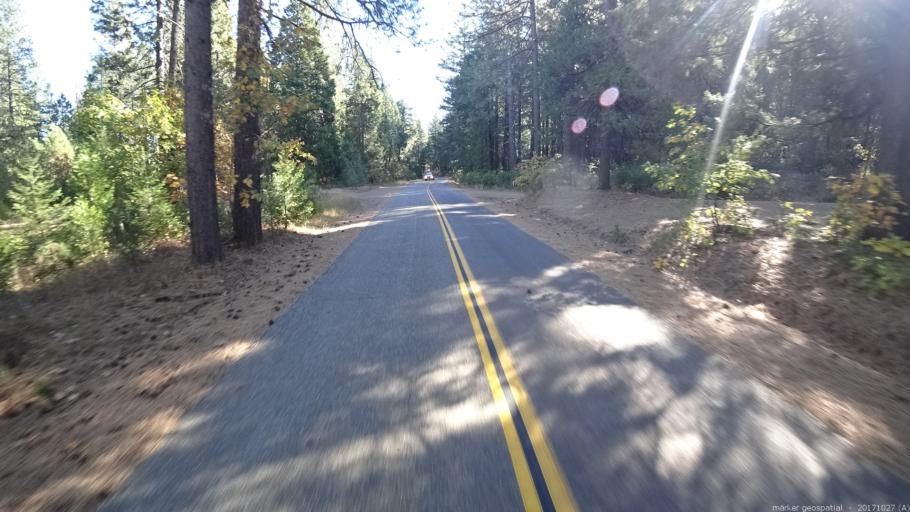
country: US
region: California
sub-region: Shasta County
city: Burney
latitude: 40.8200
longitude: -121.9647
